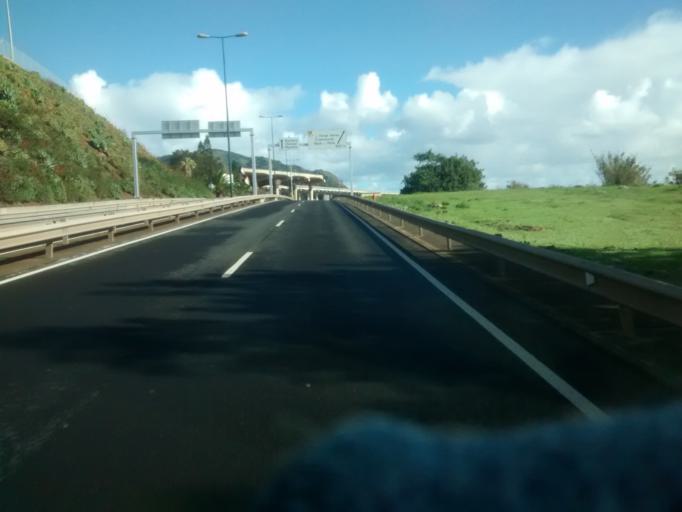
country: PT
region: Madeira
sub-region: Machico
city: Machico
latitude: 32.6949
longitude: -16.7728
